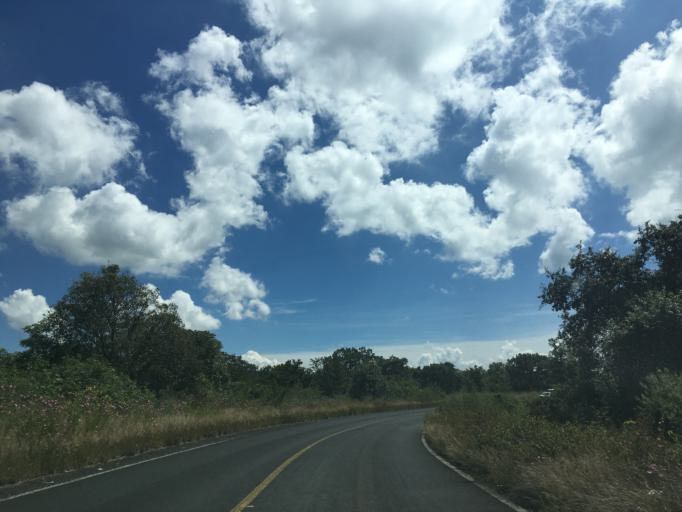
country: MX
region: Michoacan
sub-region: Morelia
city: Cuto de la Esperanza
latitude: 19.7403
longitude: -101.3518
